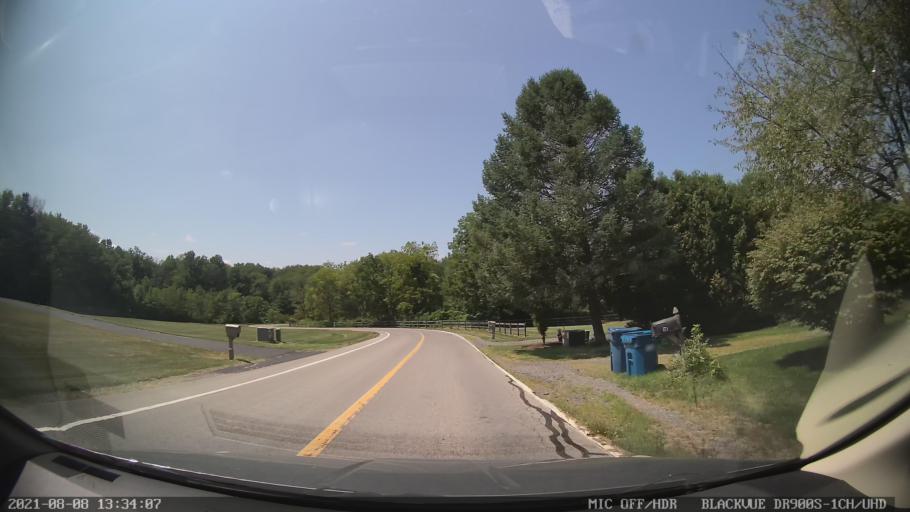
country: US
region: Pennsylvania
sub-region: Berks County
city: Fleetwood
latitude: 40.4479
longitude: -75.7629
